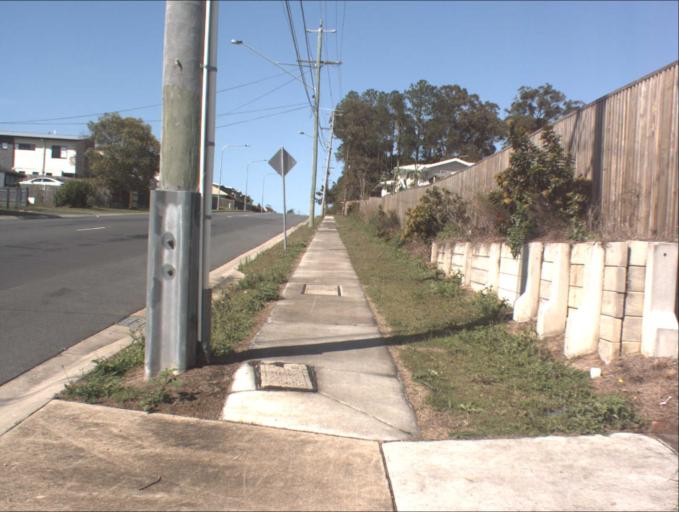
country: AU
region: Queensland
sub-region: Logan
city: Logan City
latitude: -27.6763
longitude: 153.0938
